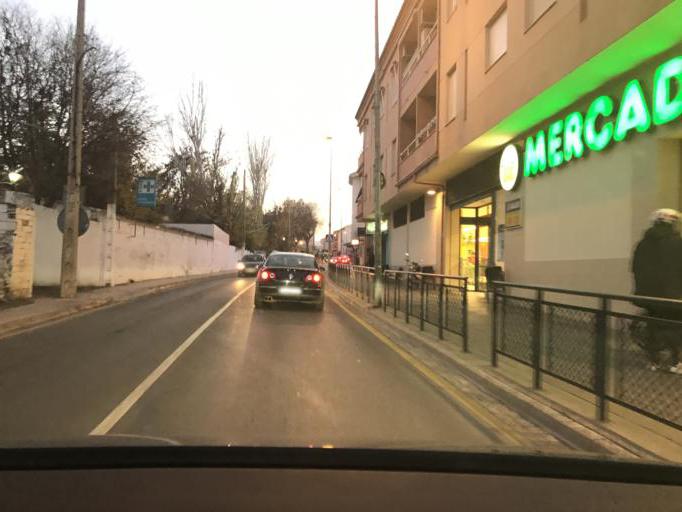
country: ES
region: Andalusia
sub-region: Provincia de Granada
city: Ogijares
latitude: 37.1249
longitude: -3.6043
